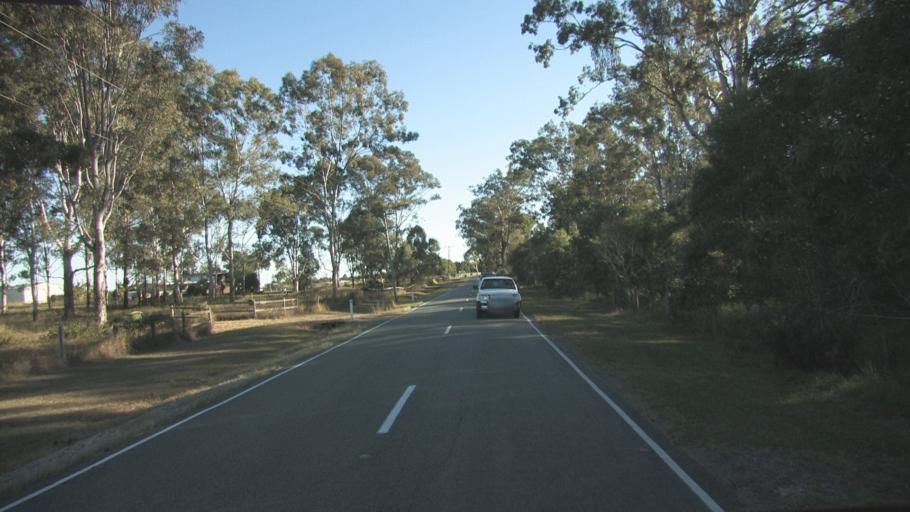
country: AU
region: Queensland
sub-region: Logan
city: Chambers Flat
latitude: -27.7541
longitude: 153.0898
